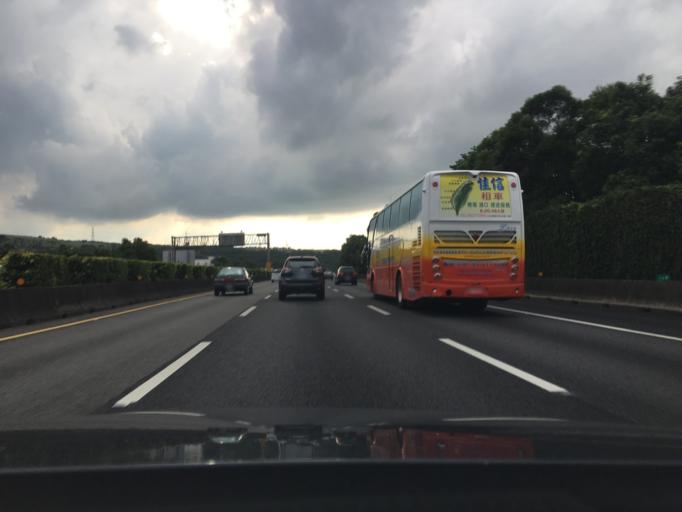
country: TW
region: Taiwan
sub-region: Hsinchu
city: Zhubei
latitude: 24.8943
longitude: 121.1278
